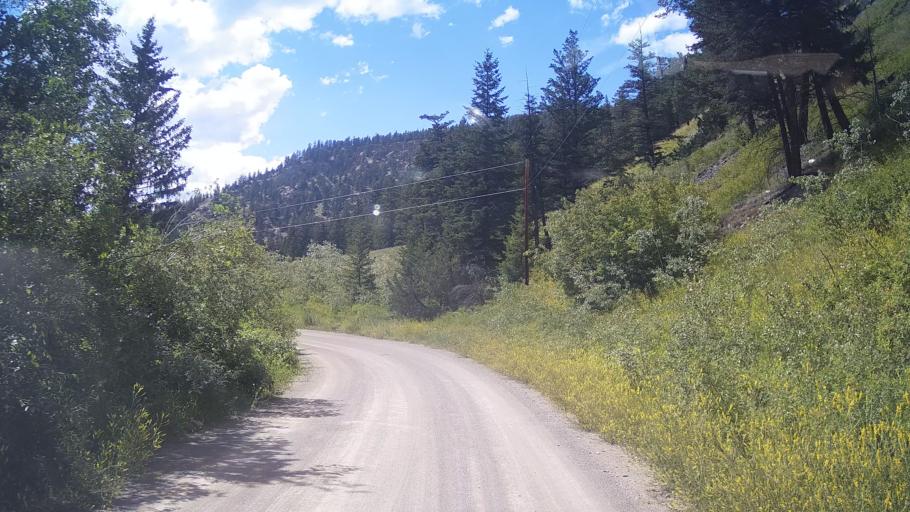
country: CA
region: British Columbia
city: Lillooet
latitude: 51.2560
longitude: -122.0038
